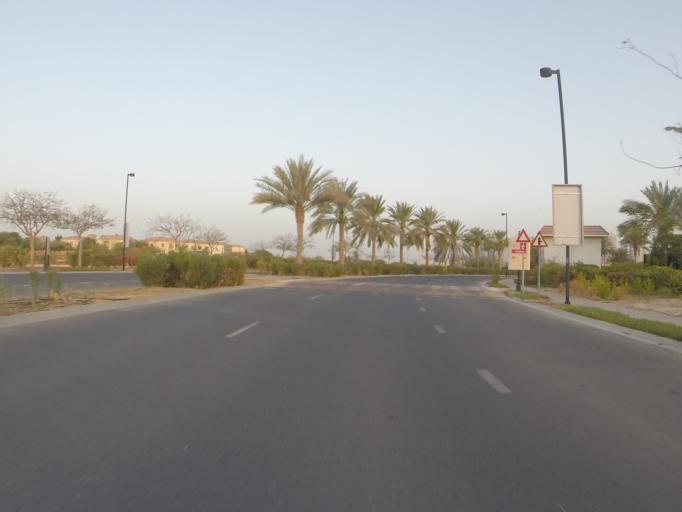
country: AE
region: Dubai
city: Dubai
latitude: 25.0547
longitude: 55.1609
